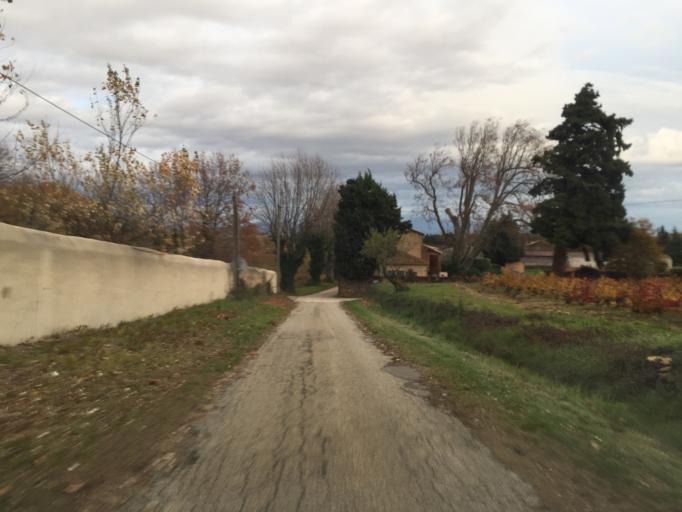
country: FR
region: Provence-Alpes-Cote d'Azur
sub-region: Departement du Vaucluse
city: Courthezon
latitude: 44.0847
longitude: 4.8580
